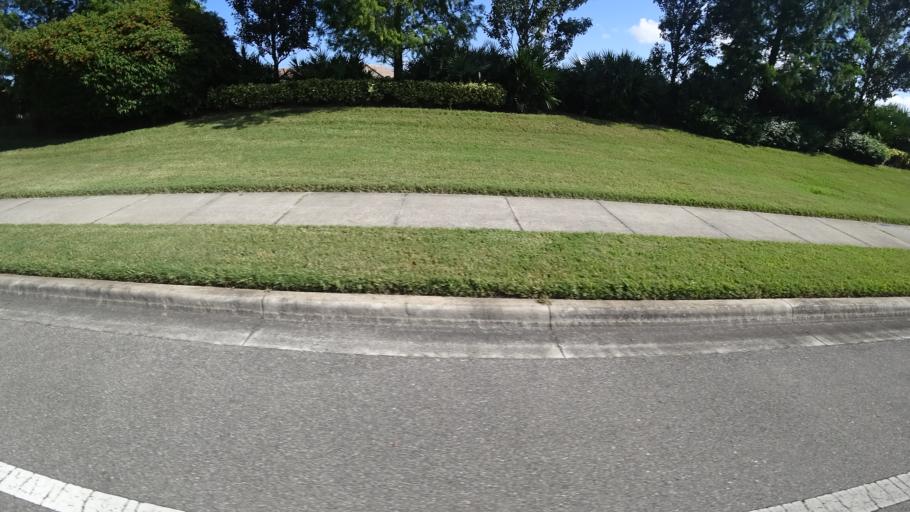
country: US
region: Florida
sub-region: Manatee County
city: Ellenton
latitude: 27.5041
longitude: -82.4690
